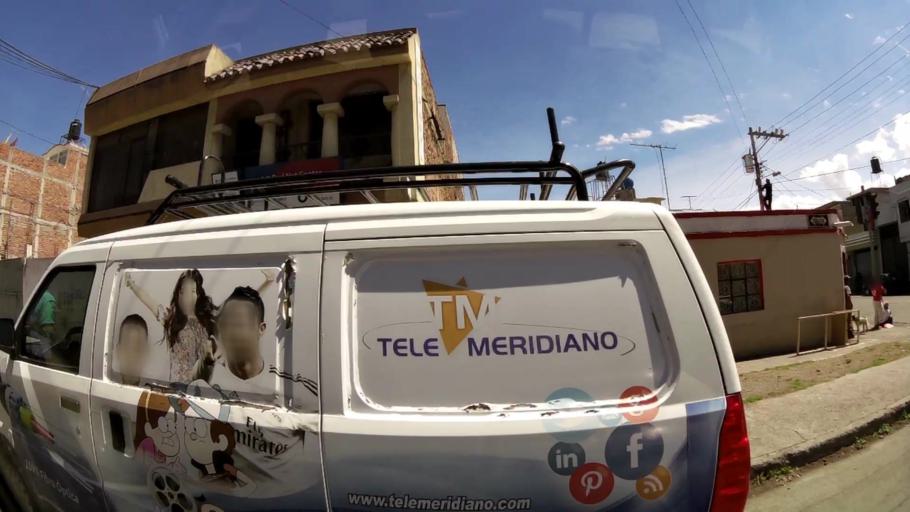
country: EC
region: Chimborazo
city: Riobamba
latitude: -1.6632
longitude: -78.6470
